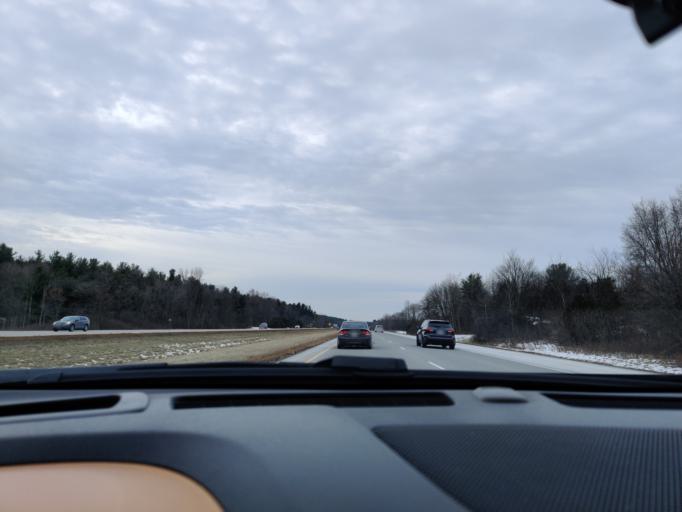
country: US
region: New York
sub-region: Jefferson County
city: Alexandria Bay
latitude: 44.4698
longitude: -75.8734
